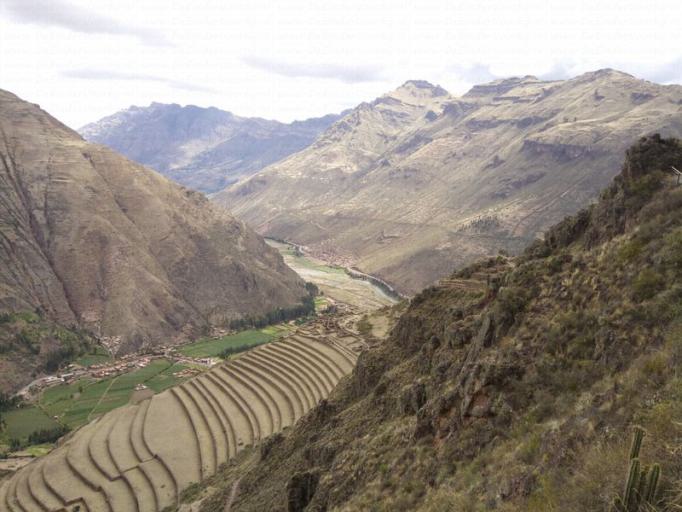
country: PE
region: Cusco
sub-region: Provincia de Calca
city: Pisac
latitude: -13.4114
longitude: -71.8433
